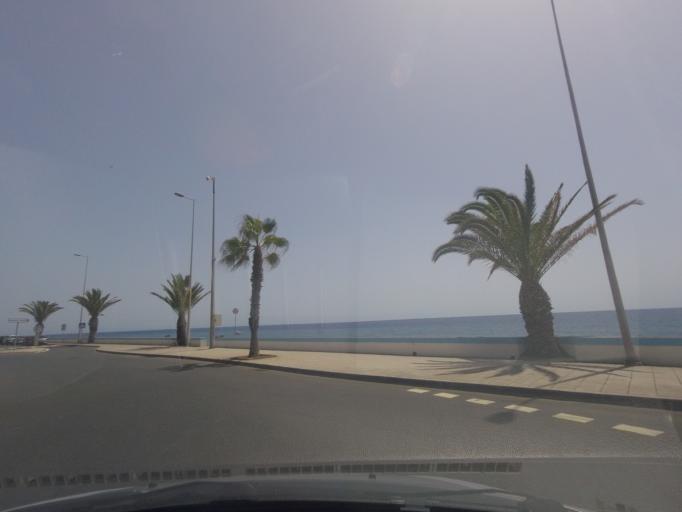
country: PT
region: Madeira
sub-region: Calheta
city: Arco da Calheta
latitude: 32.6942
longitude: -17.1265
